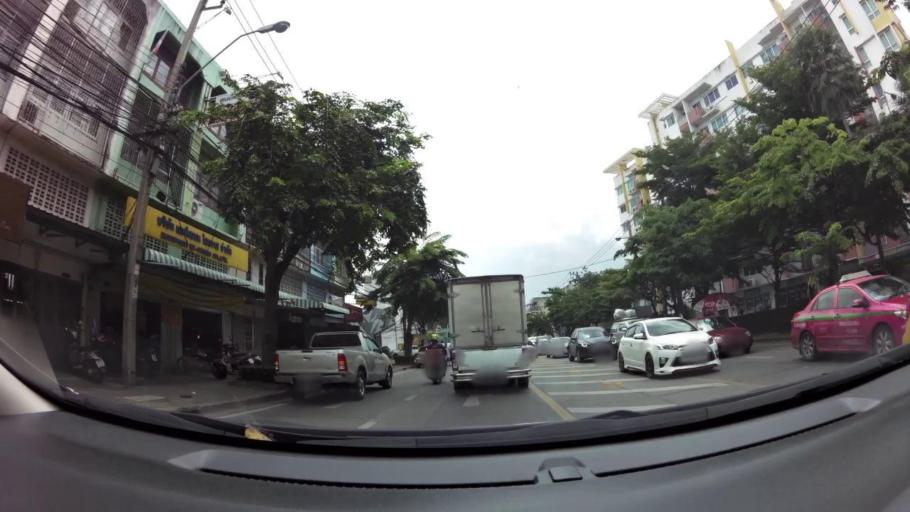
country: TH
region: Bangkok
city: Bang Na
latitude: 13.6784
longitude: 100.6217
